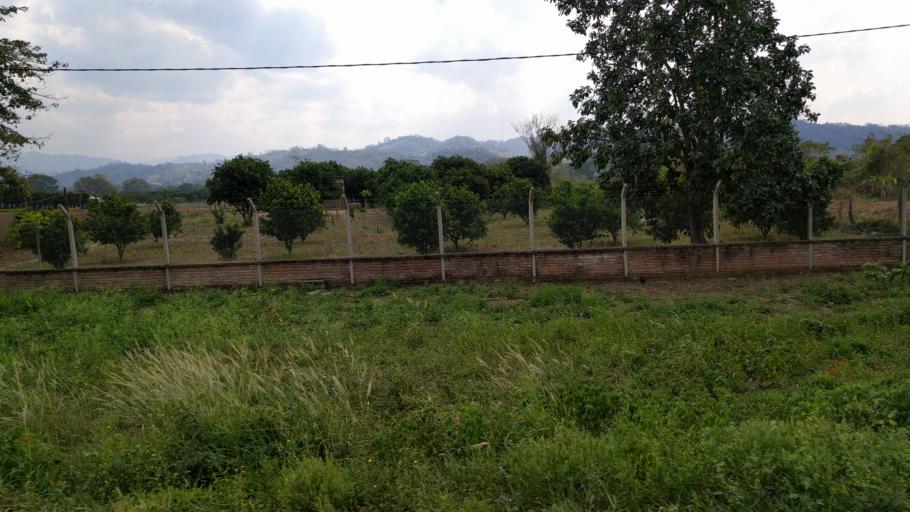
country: BO
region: Santa Cruz
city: Jorochito
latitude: -18.0442
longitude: -63.4165
